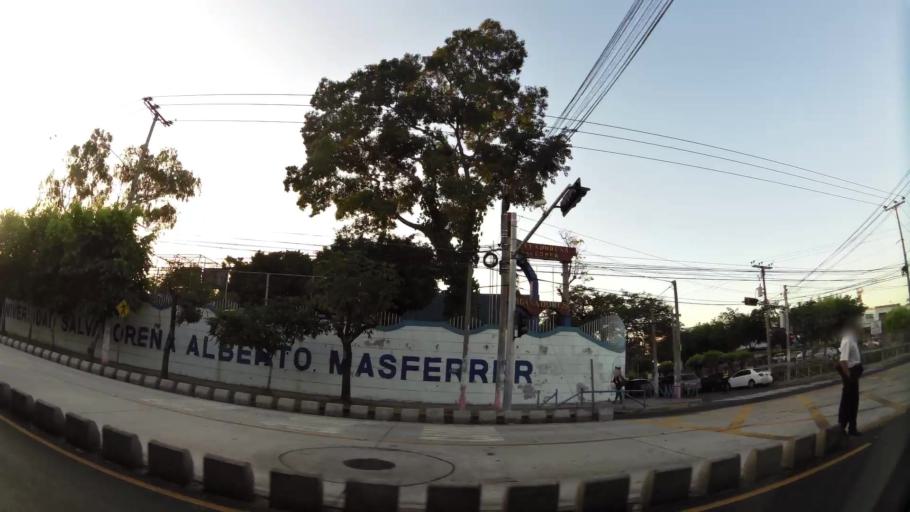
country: SV
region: San Salvador
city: San Salvador
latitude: 13.7035
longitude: -89.2009
